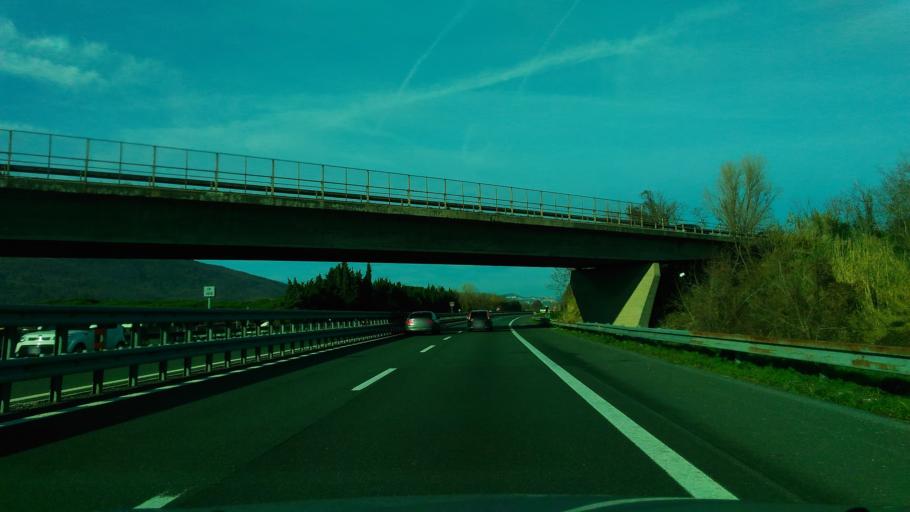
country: IT
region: Liguria
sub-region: Provincia di La Spezia
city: Ameglia
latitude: 44.0752
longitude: 9.9845
